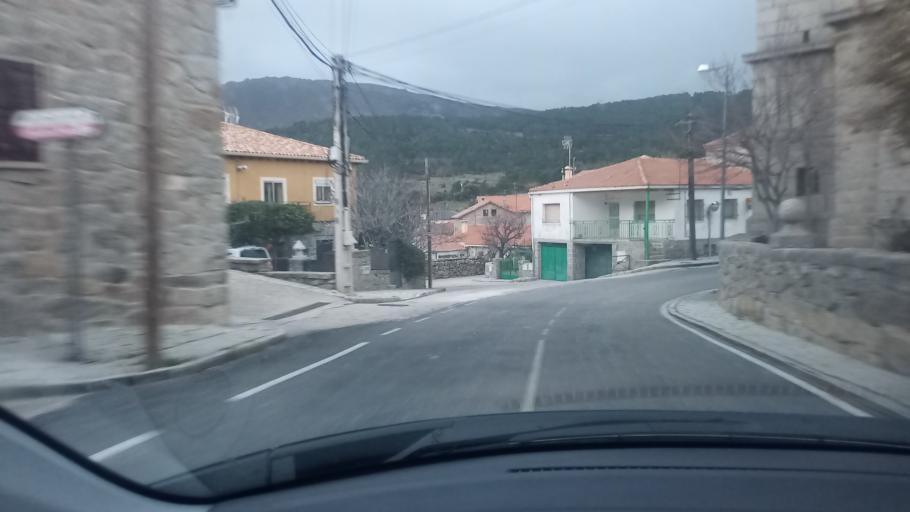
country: ES
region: Madrid
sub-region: Provincia de Madrid
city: Zarzalejo
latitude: 40.5480
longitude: -4.1824
